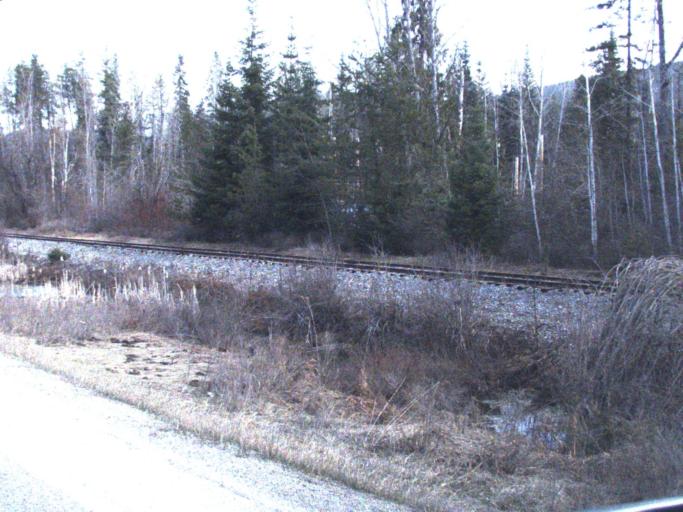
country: US
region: Washington
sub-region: Stevens County
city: Chewelah
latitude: 48.6061
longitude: -117.3635
